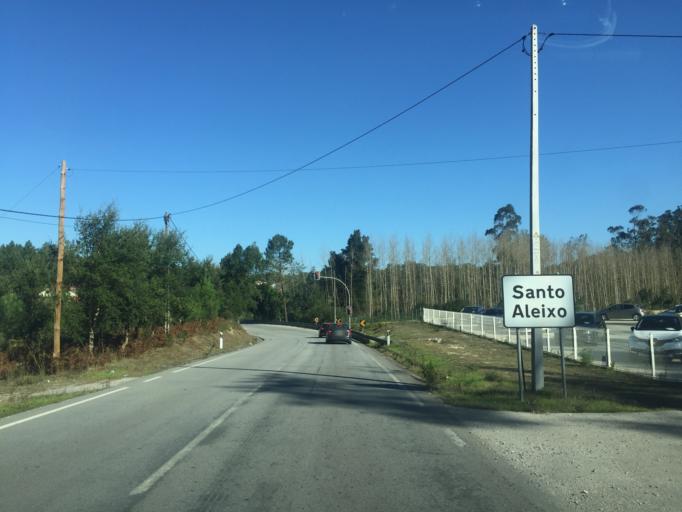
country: PT
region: Leiria
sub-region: Leiria
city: Monte Redondo
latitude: 39.9078
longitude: -8.8214
